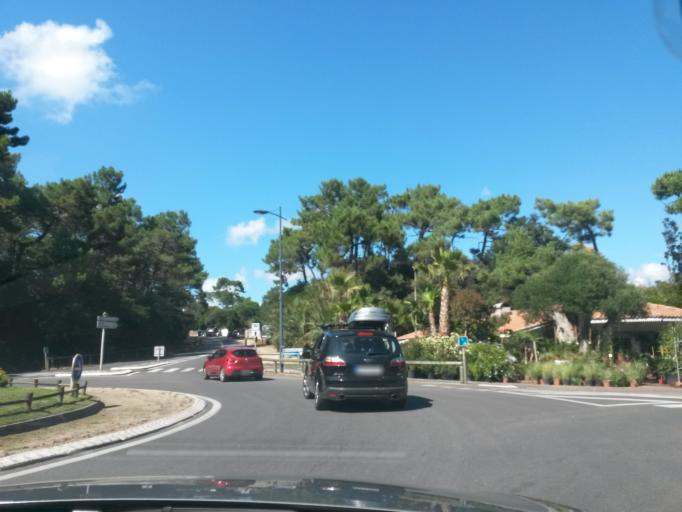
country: FR
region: Aquitaine
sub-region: Departement de la Gironde
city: Arcachon
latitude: 44.6864
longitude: -1.2376
